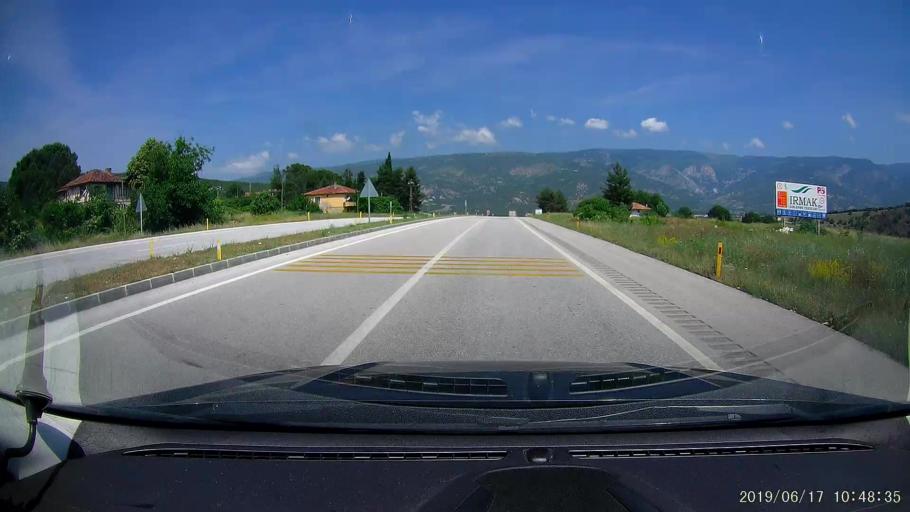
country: TR
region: Corum
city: Hacihamza
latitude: 41.0907
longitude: 34.4263
